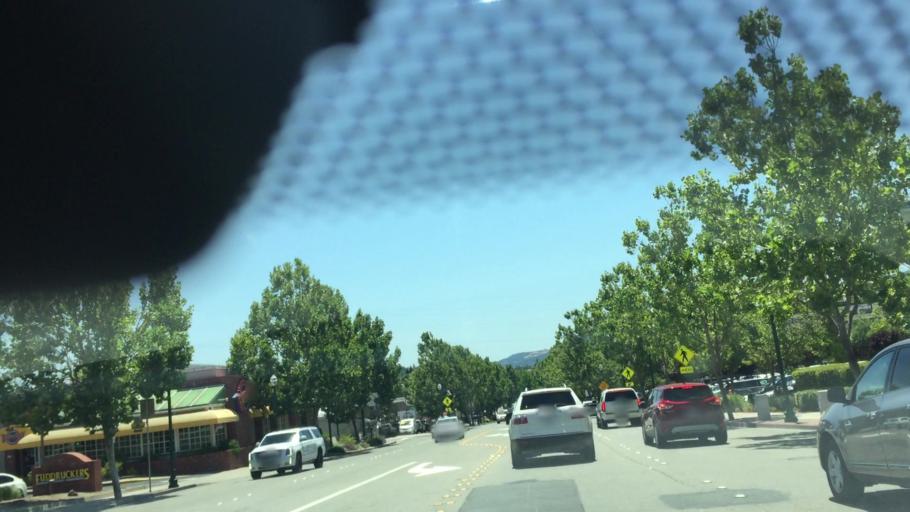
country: US
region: California
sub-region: Contra Costa County
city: Walnut Creek
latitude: 37.9057
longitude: -122.0642
